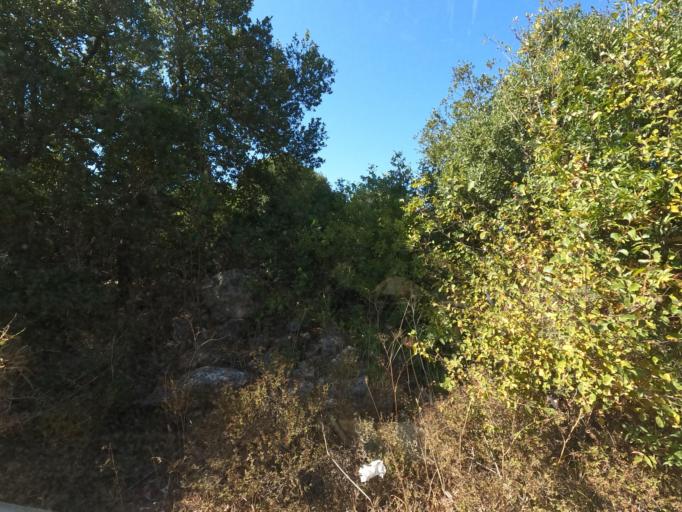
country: CY
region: Pafos
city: Polis
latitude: 34.9828
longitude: 32.4942
